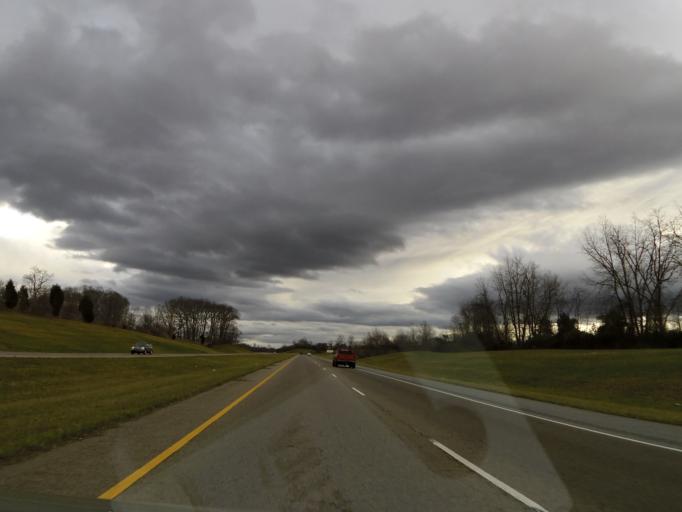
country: US
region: Tennessee
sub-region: Carter County
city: Pine Crest
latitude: 36.3131
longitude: -82.3177
